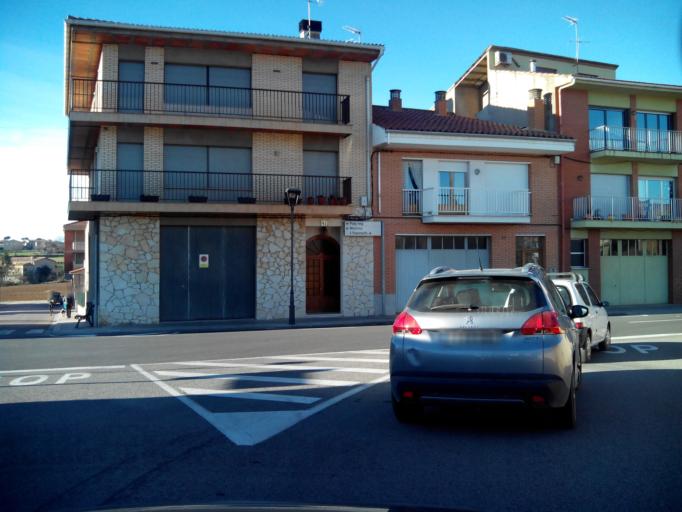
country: ES
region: Catalonia
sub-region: Provincia de Barcelona
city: Gironella
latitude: 42.0115
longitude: 1.8437
